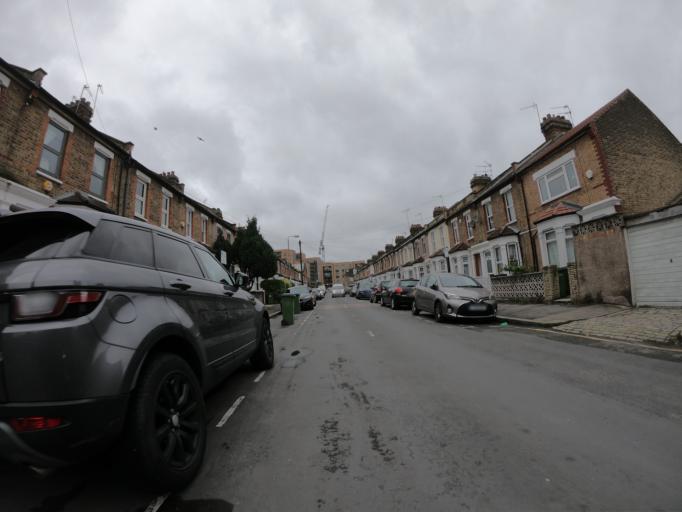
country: GB
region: England
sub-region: Greater London
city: Blackheath
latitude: 51.4863
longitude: 0.0271
